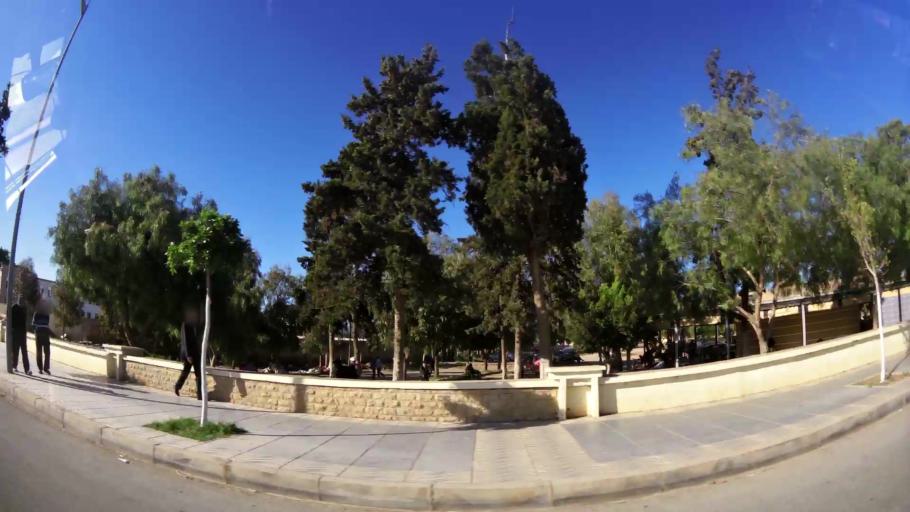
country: MA
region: Oriental
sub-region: Berkane-Taourirt
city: Ahfir
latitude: 34.9478
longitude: -2.1049
